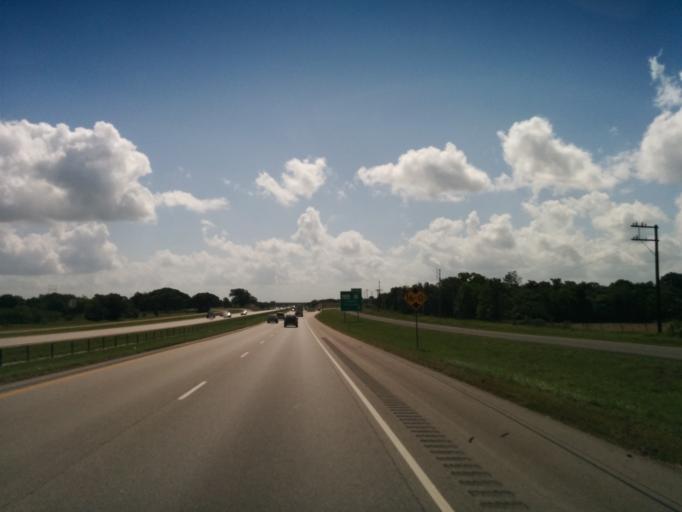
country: US
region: Texas
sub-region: Colorado County
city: Columbus
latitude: 29.6933
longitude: -96.5974
